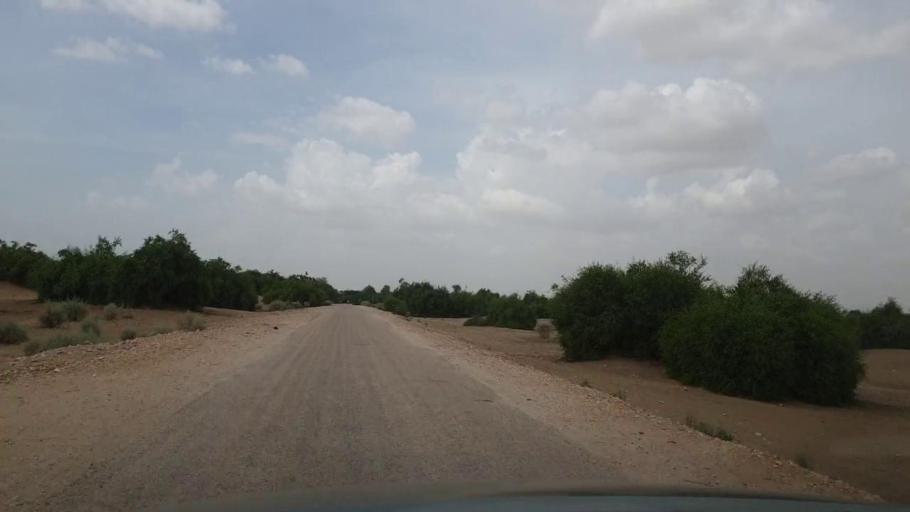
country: PK
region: Sindh
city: Kot Diji
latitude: 27.2185
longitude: 69.0839
